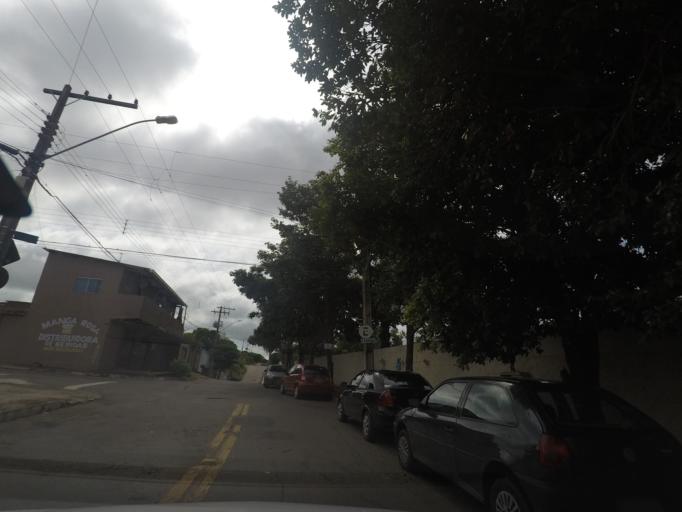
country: BR
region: Goias
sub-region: Goiania
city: Goiania
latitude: -16.6628
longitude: -49.1951
